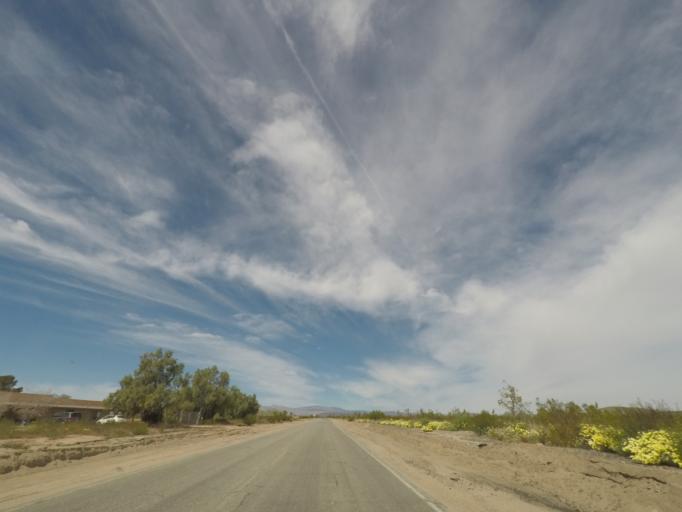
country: US
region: California
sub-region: San Bernardino County
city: Joshua Tree
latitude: 34.1929
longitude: -116.3399
